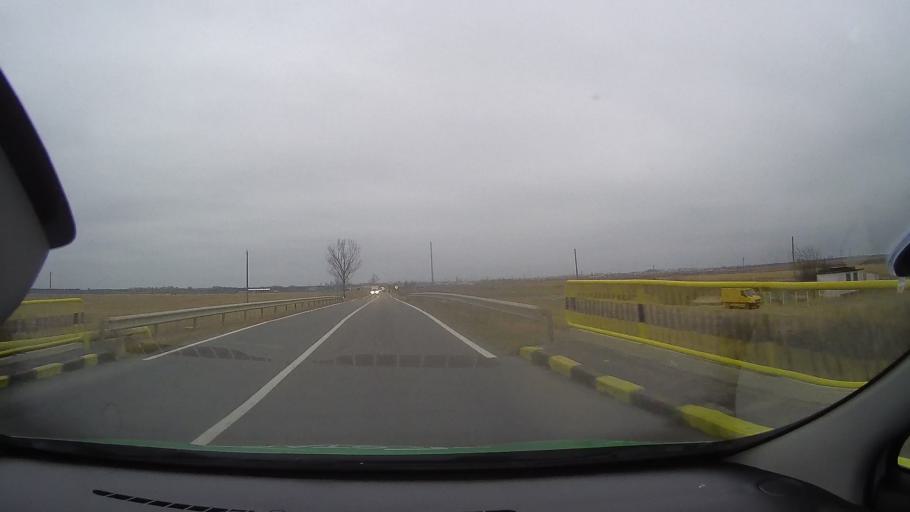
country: RO
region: Ialomita
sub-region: Comuna Slobozia
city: Slobozia
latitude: 44.5904
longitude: 27.3903
